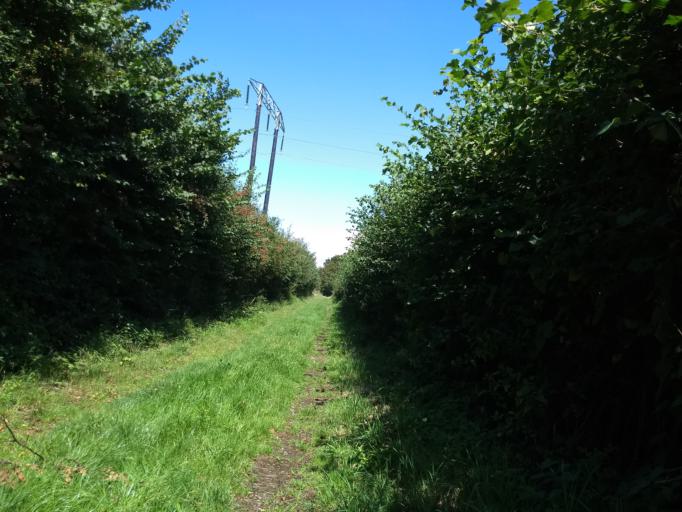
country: GB
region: England
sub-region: Isle of Wight
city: Northwood
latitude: 50.7349
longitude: -1.3020
